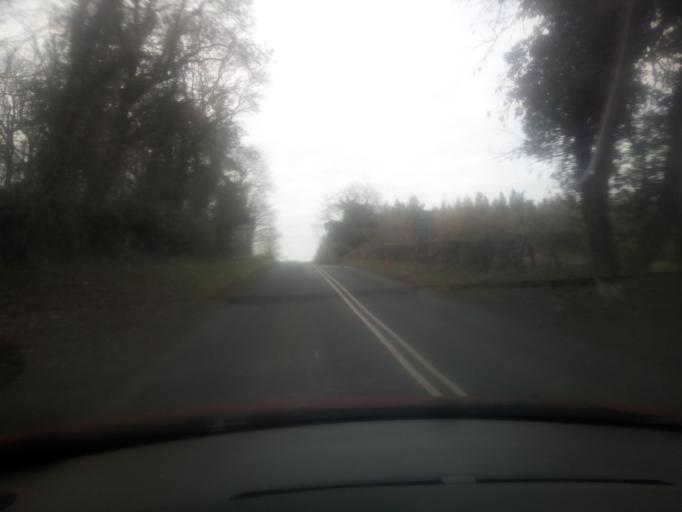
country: GB
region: England
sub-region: Darlington
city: Denton
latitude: 54.5748
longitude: -1.6777
